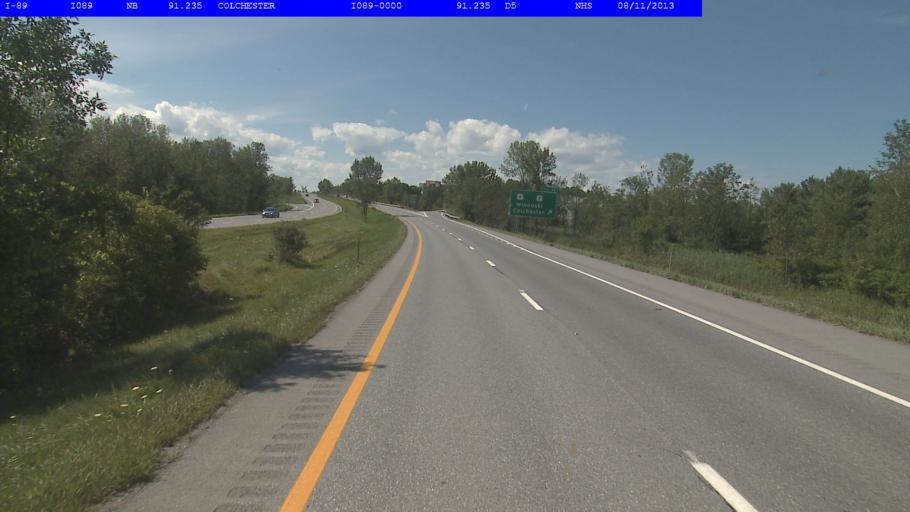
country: US
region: Vermont
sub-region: Chittenden County
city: Winooski
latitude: 44.5037
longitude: -73.1768
